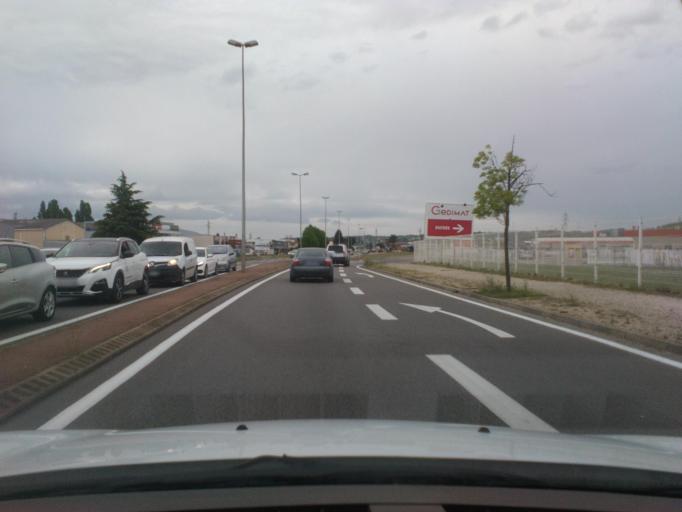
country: FR
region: Rhone-Alpes
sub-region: Departement de l'Isere
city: Salaise-sur-Sanne
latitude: 45.3459
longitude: 4.8035
